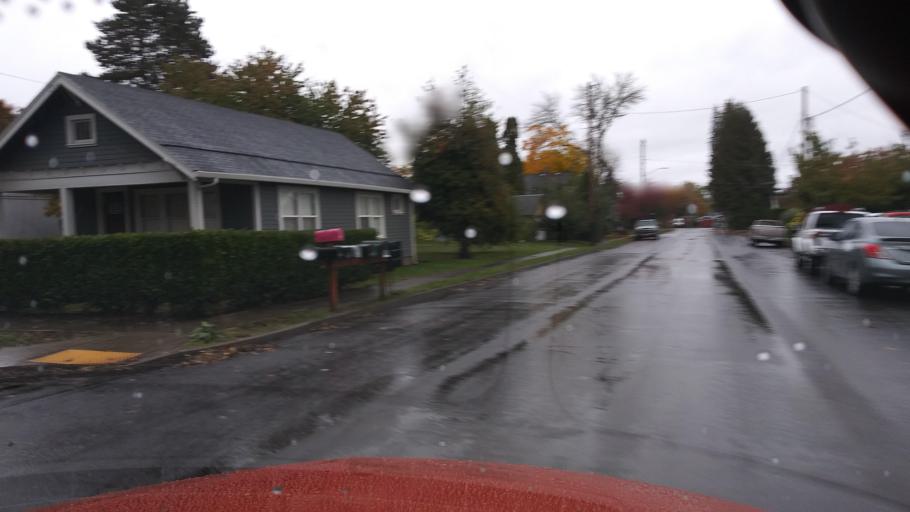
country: US
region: Oregon
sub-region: Washington County
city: Cornelius
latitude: 45.5184
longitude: -123.0547
